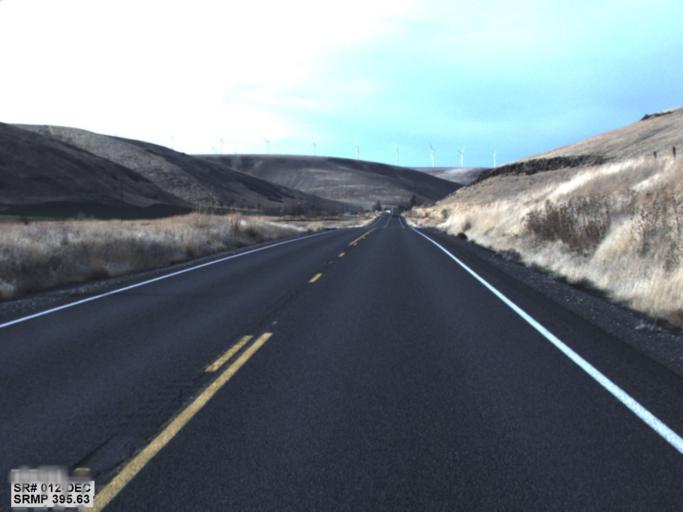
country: US
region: Washington
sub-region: Garfield County
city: Pomeroy
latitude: 46.4847
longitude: -117.7462
